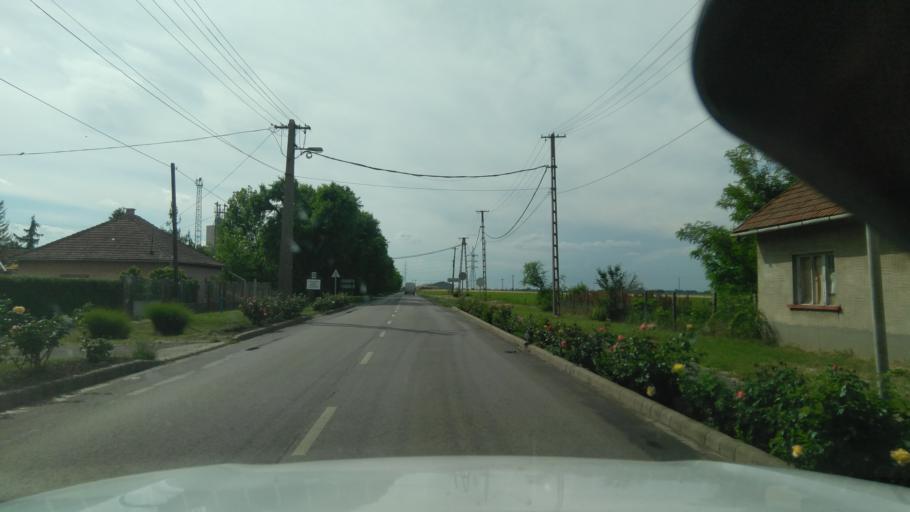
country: HU
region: Bekes
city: Medgyesegyhaza
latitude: 46.5034
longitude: 21.0165
